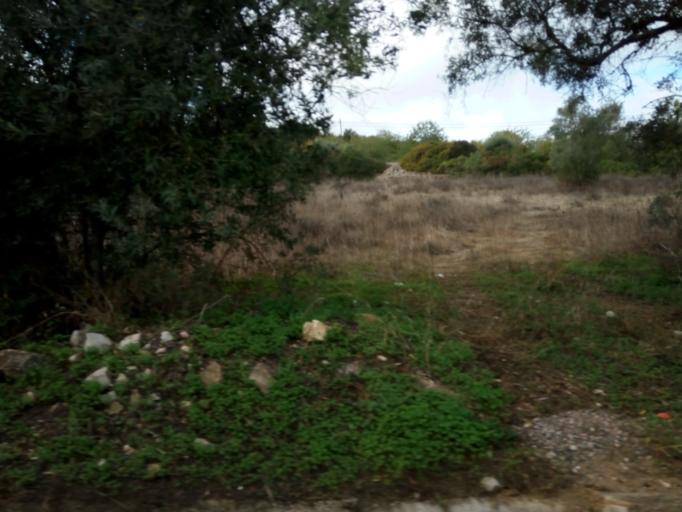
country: PT
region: Faro
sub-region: Faro
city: Santa Barbara de Nexe
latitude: 37.1241
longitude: -7.9557
